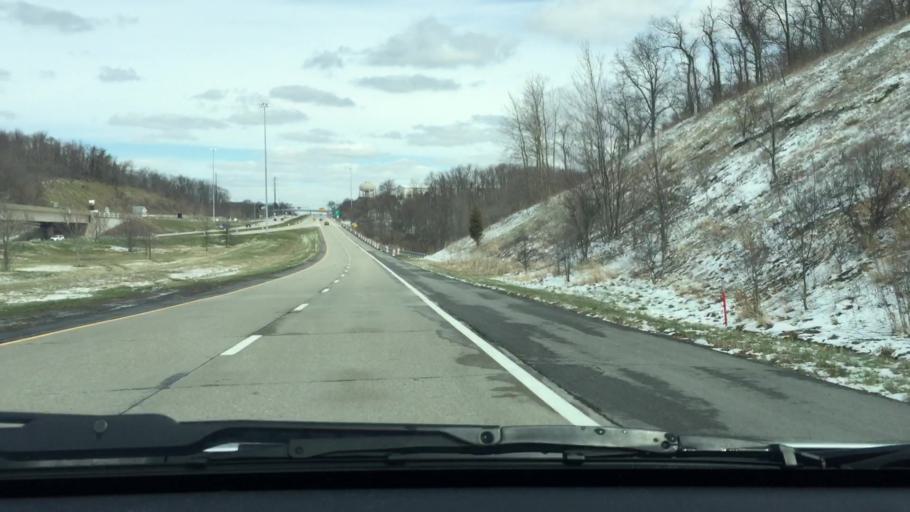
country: US
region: Pennsylvania
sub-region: Allegheny County
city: Carnot-Moon
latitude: 40.5210
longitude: -80.2723
